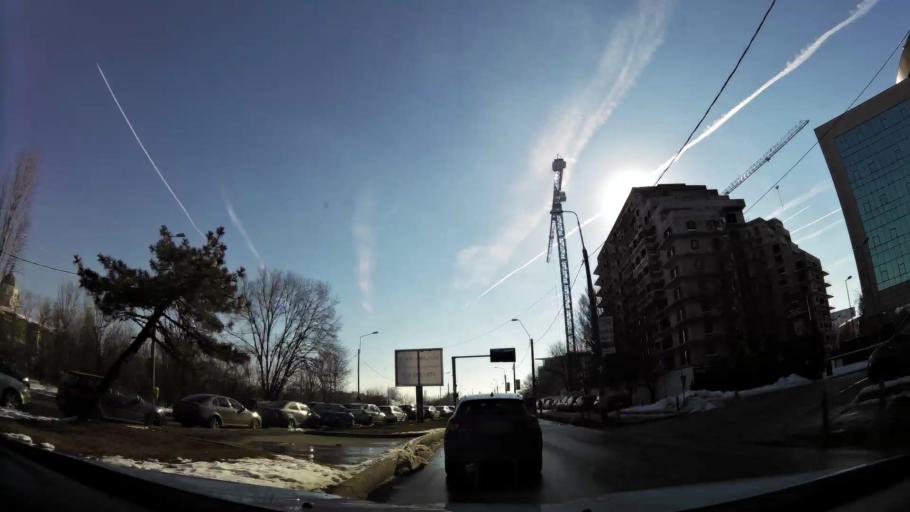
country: RO
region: Bucuresti
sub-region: Municipiul Bucuresti
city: Bucuresti
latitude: 44.4312
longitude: 26.0596
